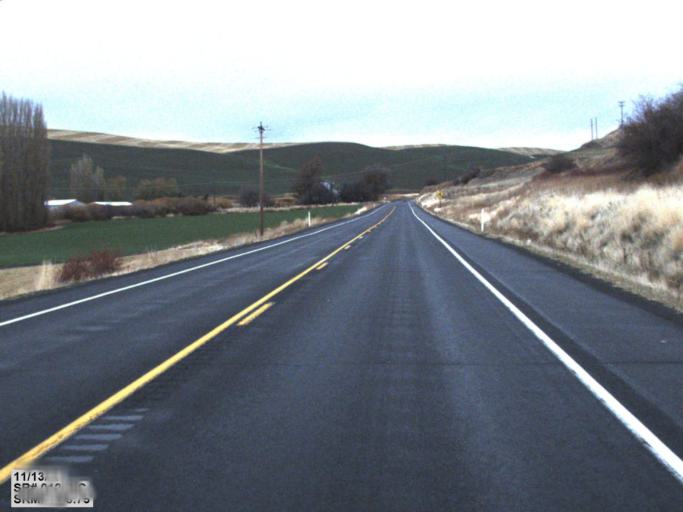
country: US
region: Washington
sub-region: Columbia County
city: Dayton
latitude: 46.3390
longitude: -117.9794
